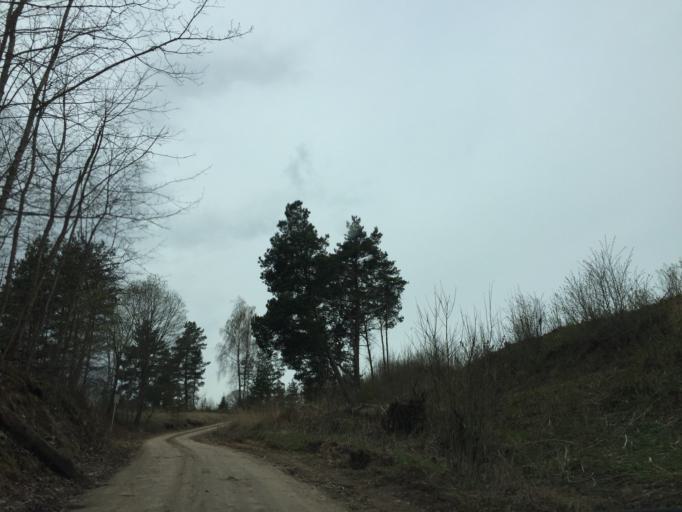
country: LV
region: Priekuli
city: Priekuli
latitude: 57.3321
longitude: 25.3856
